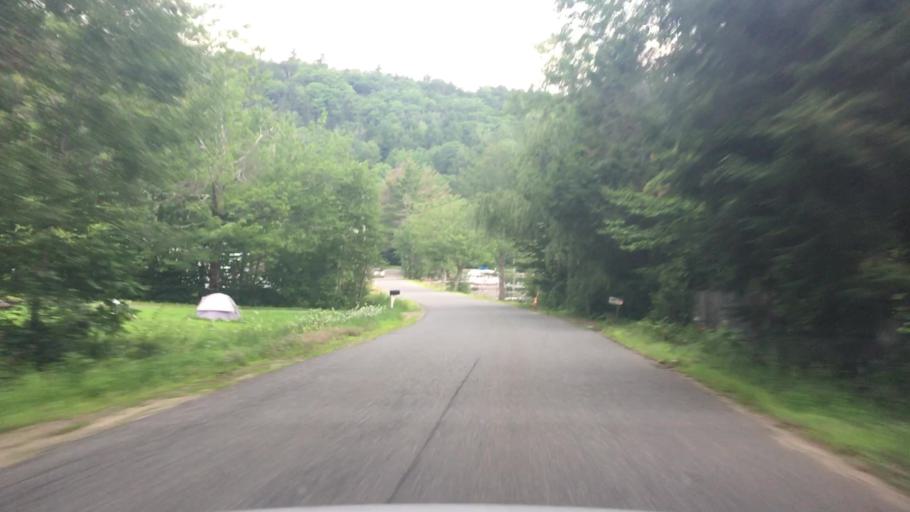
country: US
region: Maine
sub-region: Knox County
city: Washington
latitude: 44.3738
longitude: -69.3503
